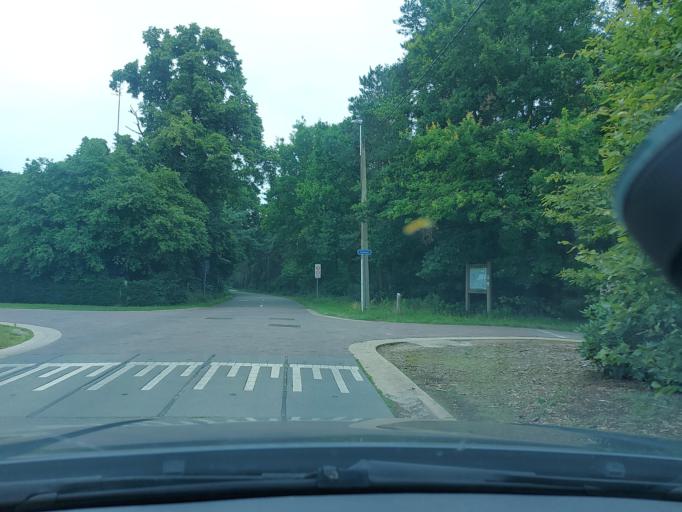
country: BE
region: Flanders
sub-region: Provincie Antwerpen
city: Balen
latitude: 51.1739
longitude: 5.2125
